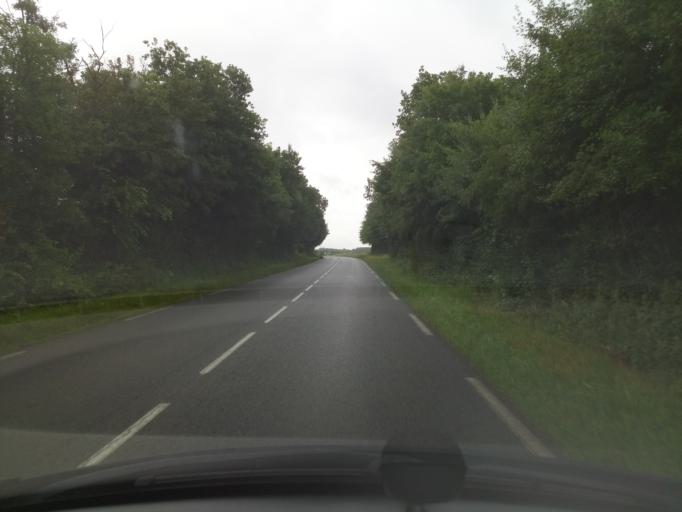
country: FR
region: Poitou-Charentes
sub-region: Departement de la Charente-Maritime
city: Courcon
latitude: 46.1780
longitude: -0.8474
